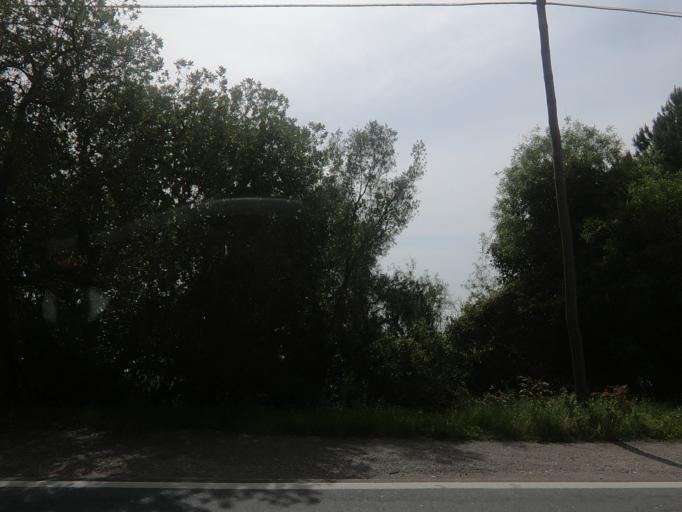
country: PT
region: Setubal
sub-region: Setubal
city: Setubal
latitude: 38.4993
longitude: -8.9297
